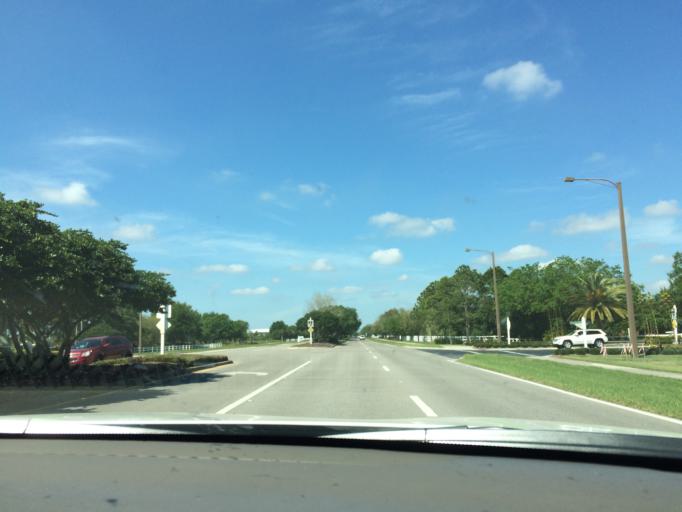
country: US
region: Florida
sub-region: Sarasota County
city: The Meadows
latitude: 27.3865
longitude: -82.4235
